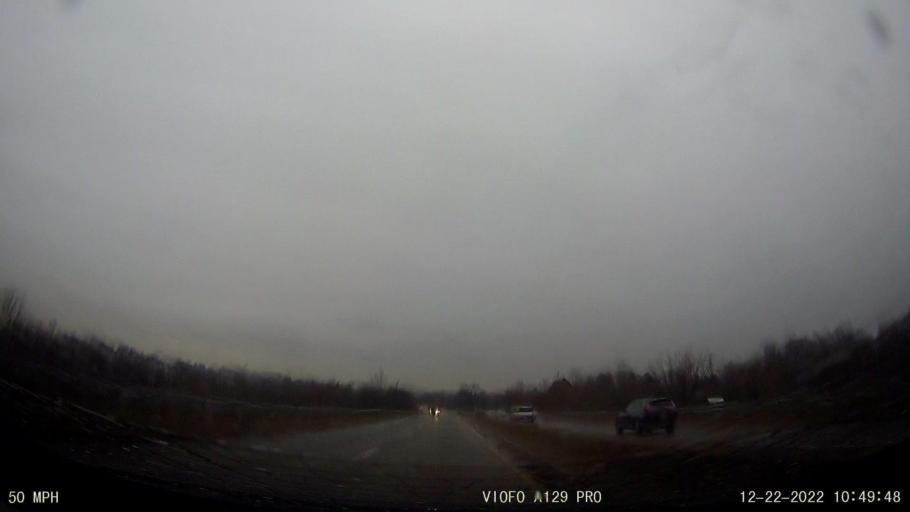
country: US
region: Pennsylvania
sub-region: Montgomery County
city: Bridgeport
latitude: 40.1100
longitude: -75.3506
